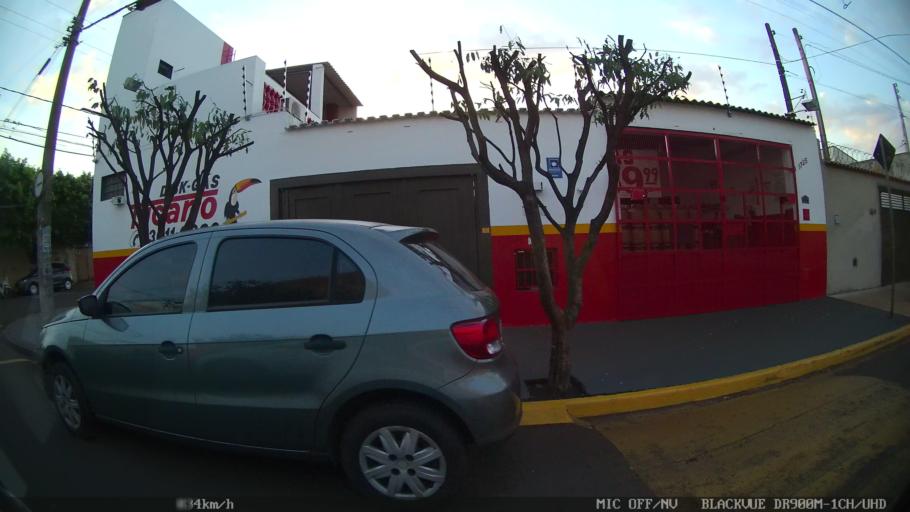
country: BR
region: Sao Paulo
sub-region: Ribeirao Preto
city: Ribeirao Preto
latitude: -21.1453
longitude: -47.8217
